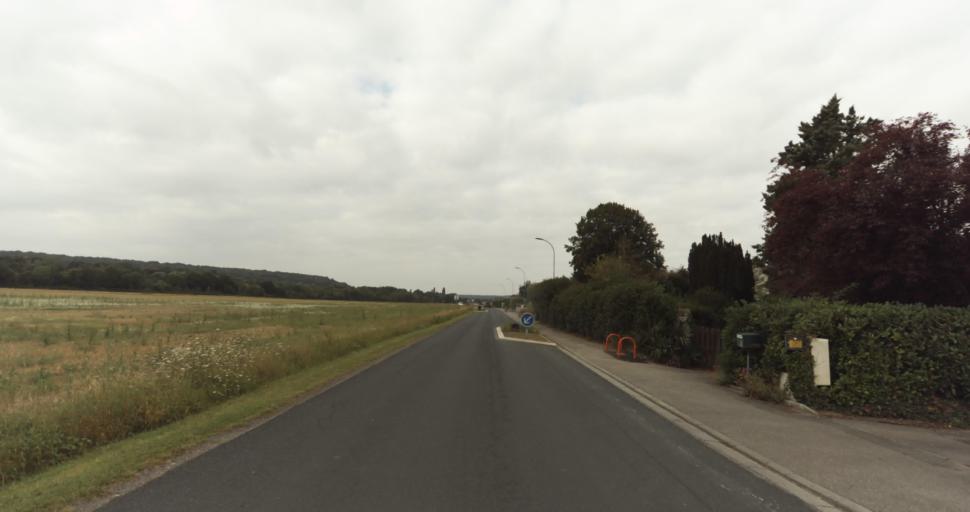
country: FR
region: Haute-Normandie
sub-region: Departement de l'Eure
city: Croth
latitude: 48.8440
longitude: 1.3720
